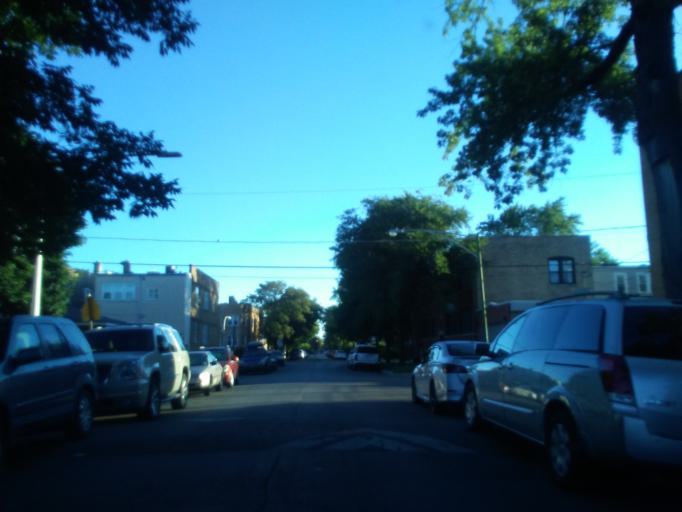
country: US
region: Illinois
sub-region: Cook County
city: Elmwood Park
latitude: 41.9362
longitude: -87.7541
